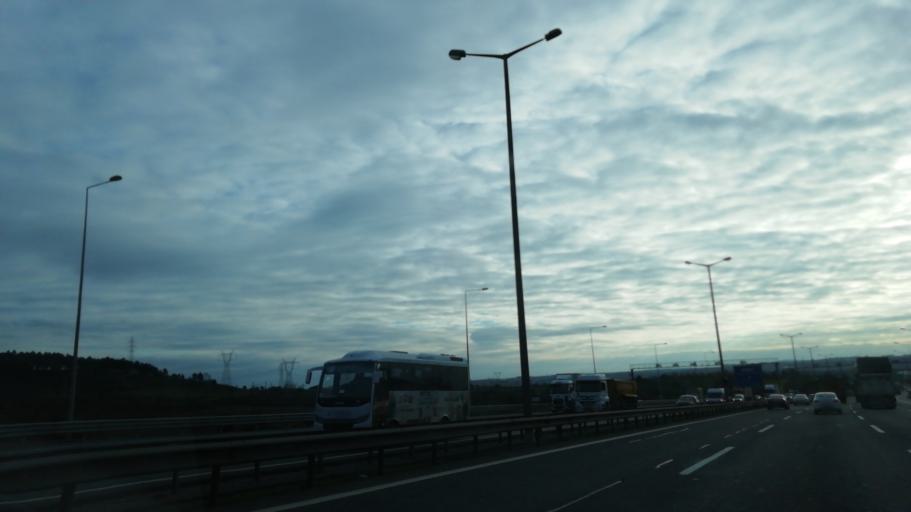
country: TR
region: Istanbul
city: Sultanbeyli
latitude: 40.9401
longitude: 29.3248
